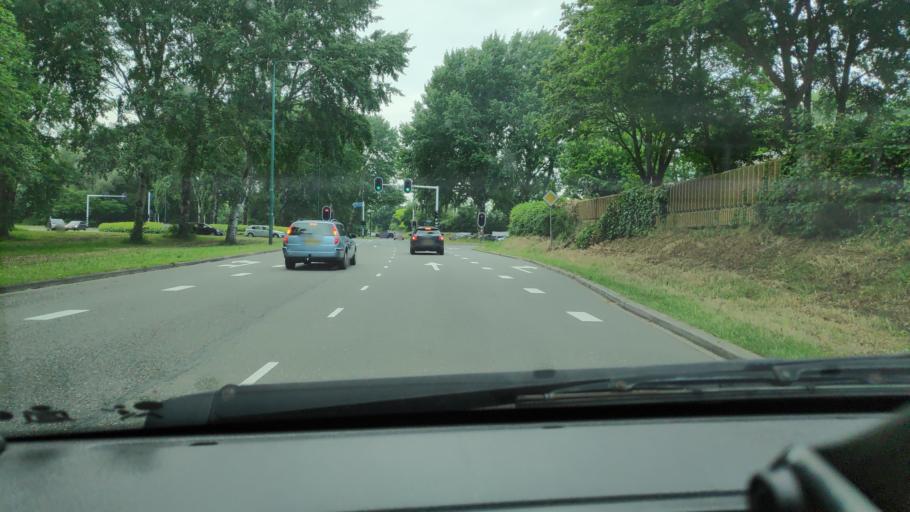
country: NL
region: Utrecht
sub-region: Stichtse Vecht
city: Spechtenkamp
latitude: 52.1274
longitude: 5.0285
